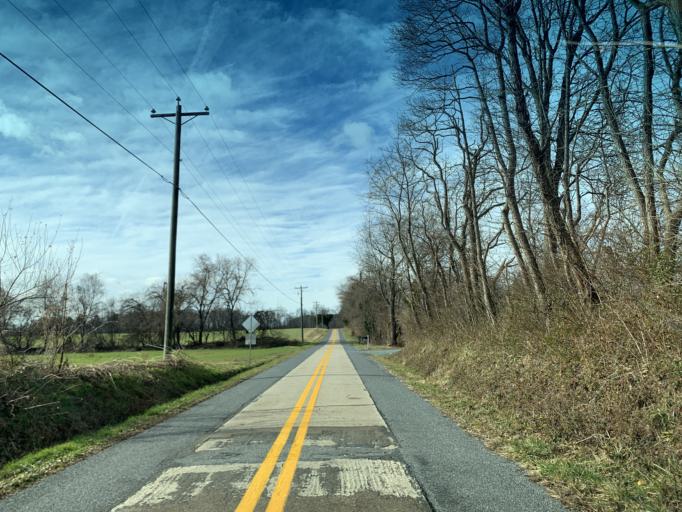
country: US
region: Maryland
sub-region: Harford County
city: Aberdeen Proving Ground
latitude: 39.3495
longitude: -76.0572
